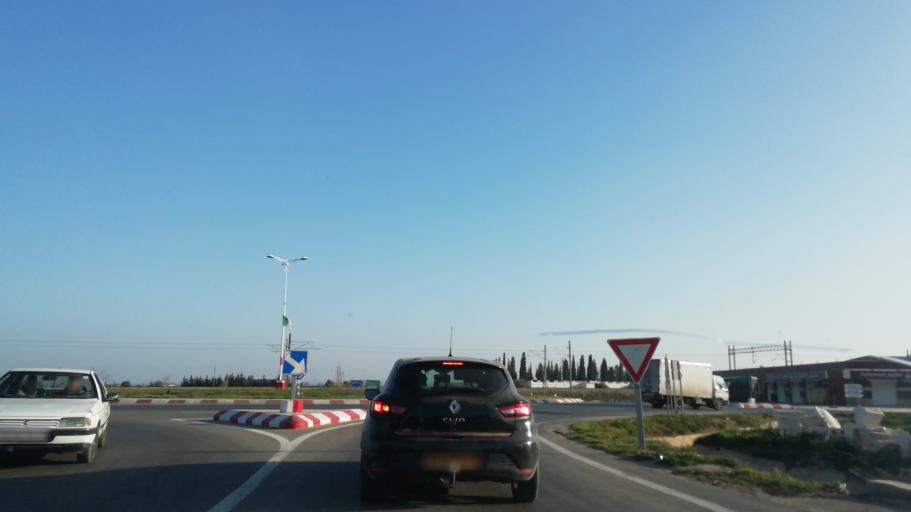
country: DZ
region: Sidi Bel Abbes
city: Sidi Bel Abbes
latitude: 35.1673
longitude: -0.6869
